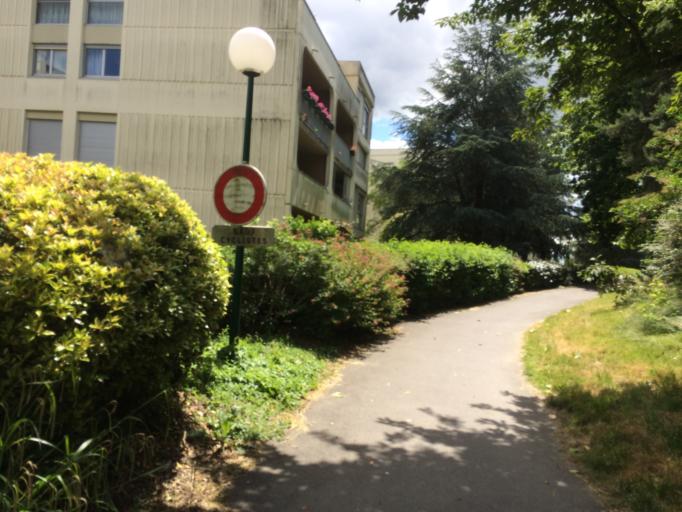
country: FR
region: Ile-de-France
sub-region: Departement de l'Essonne
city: Les Ulis
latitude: 48.6805
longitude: 2.1707
